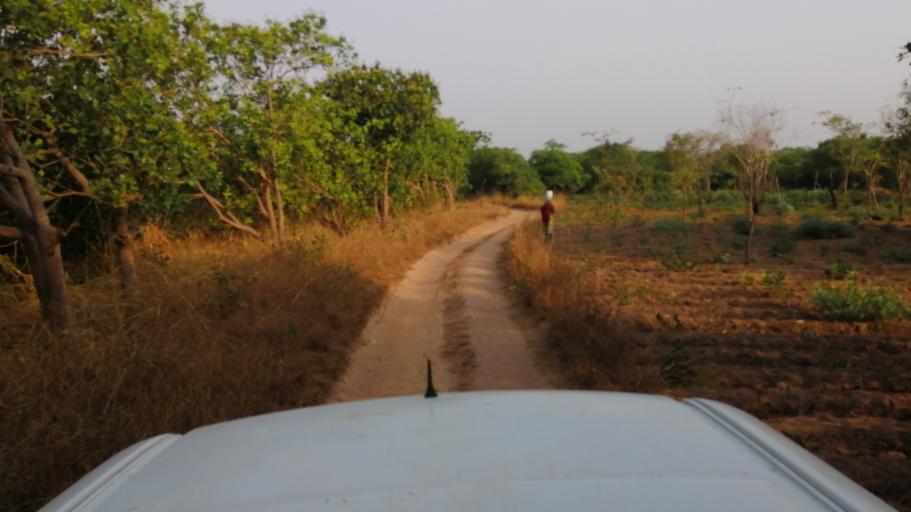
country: GW
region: Bissau
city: Bissau
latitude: 11.9800
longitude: -15.4679
